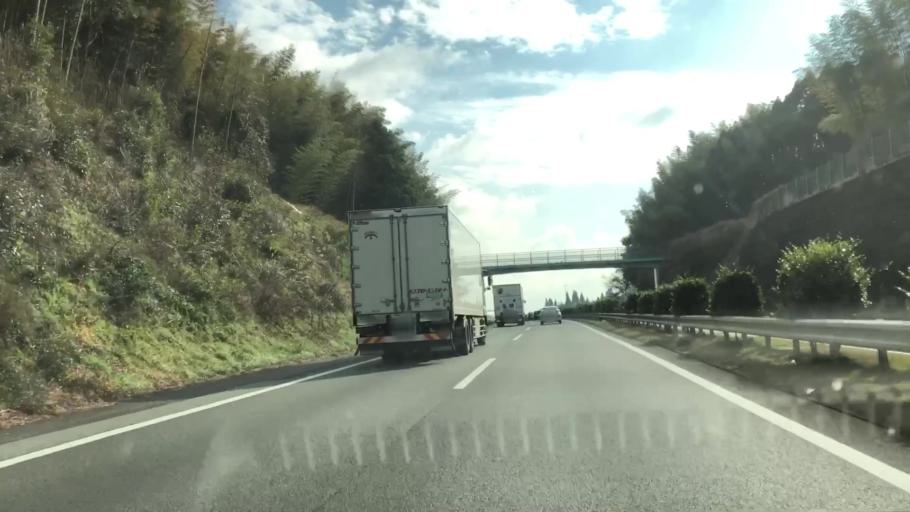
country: JP
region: Fukuoka
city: Setakamachi-takayanagi
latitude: 33.0909
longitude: 130.5389
